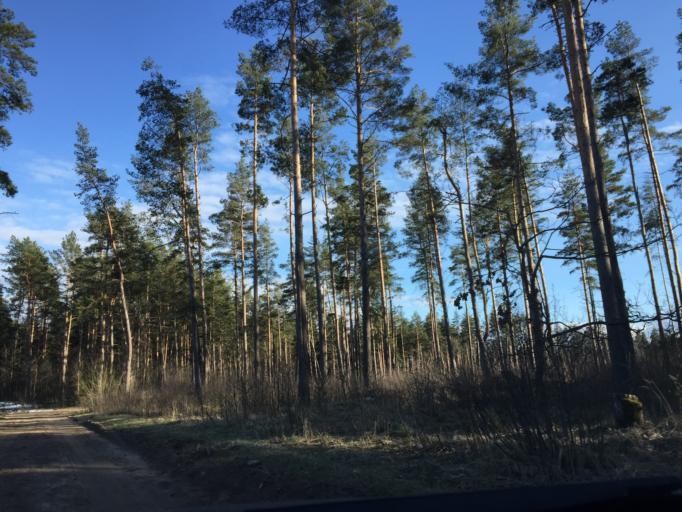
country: LV
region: Kekava
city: Kekava
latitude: 56.8440
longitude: 24.1957
